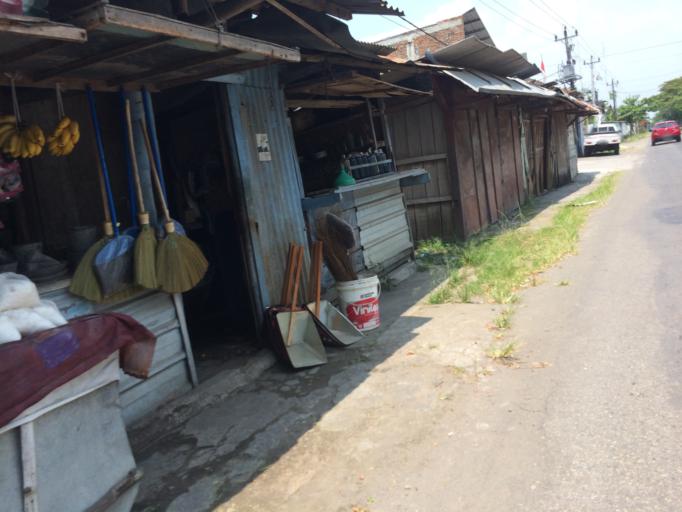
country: ID
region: Central Java
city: Grogol
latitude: -7.6158
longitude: 110.8226
